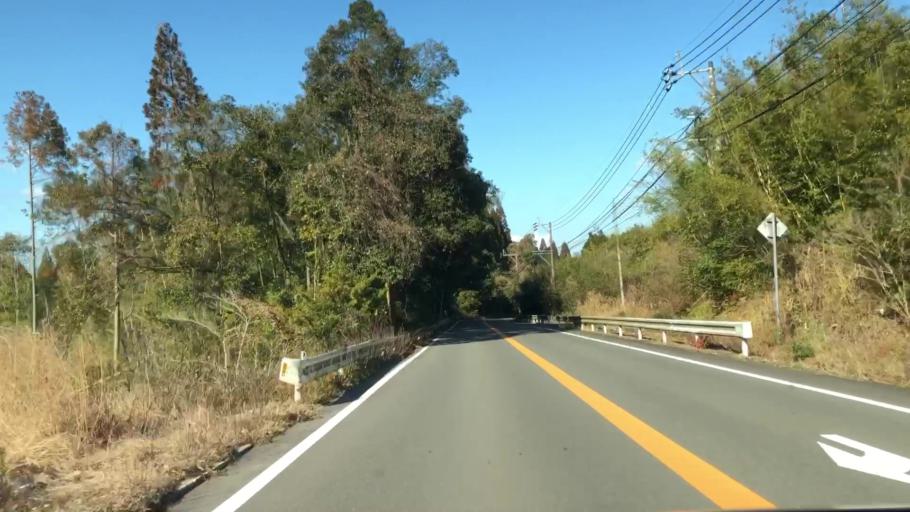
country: JP
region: Kagoshima
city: Satsumasendai
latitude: 31.8541
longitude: 130.4293
